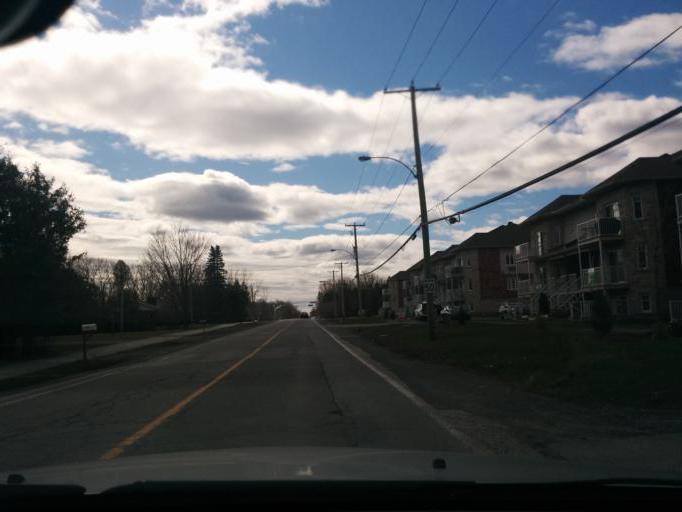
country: CA
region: Ontario
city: Bells Corners
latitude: 45.4126
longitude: -75.8057
